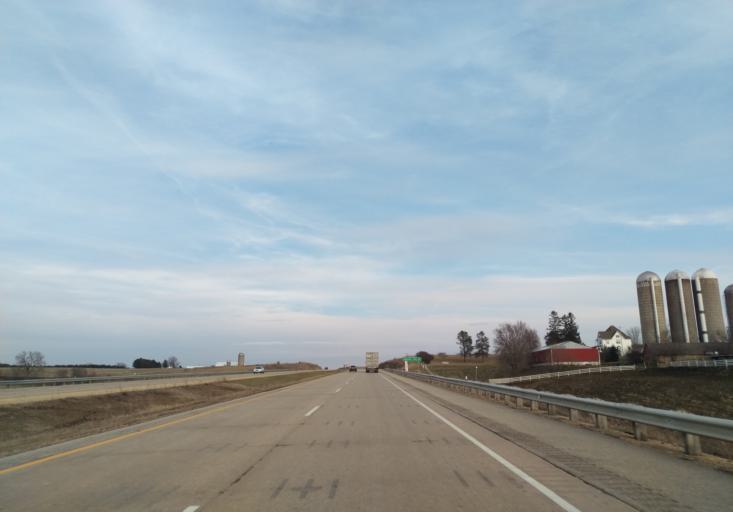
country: US
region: Wisconsin
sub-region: Iowa County
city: Barneveld
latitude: 43.0096
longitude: -89.8682
